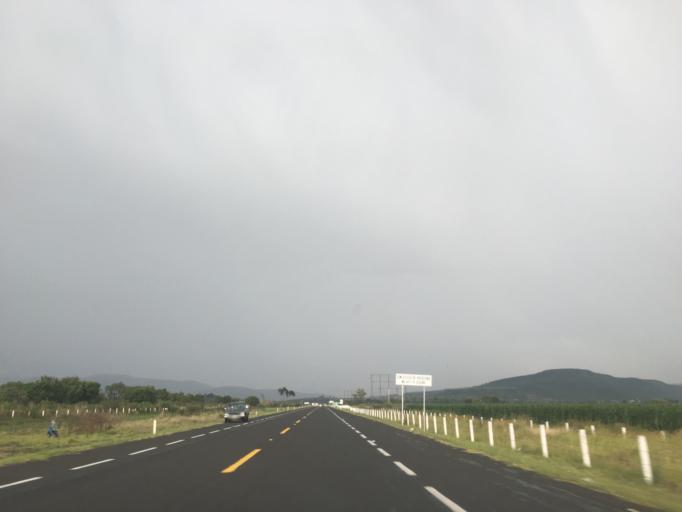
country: MX
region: Michoacan
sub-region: Alvaro Obregon
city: Lazaro Cardenas (La Purisima)
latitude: 19.8397
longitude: -101.0102
